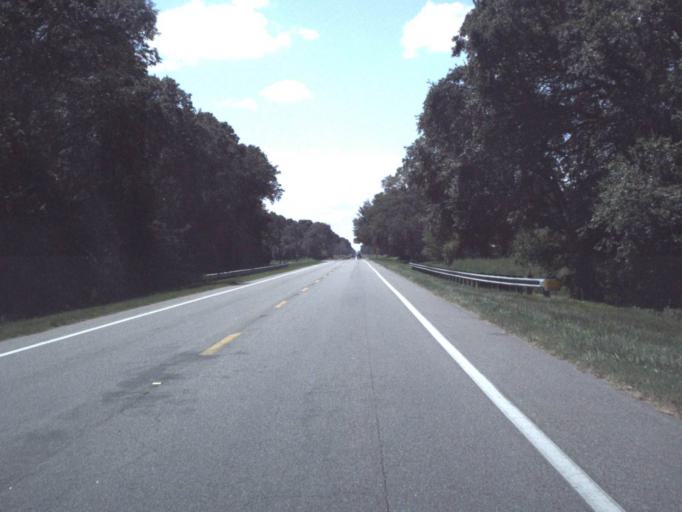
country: US
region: Florida
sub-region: Lafayette County
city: Mayo
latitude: 30.0115
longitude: -83.0347
